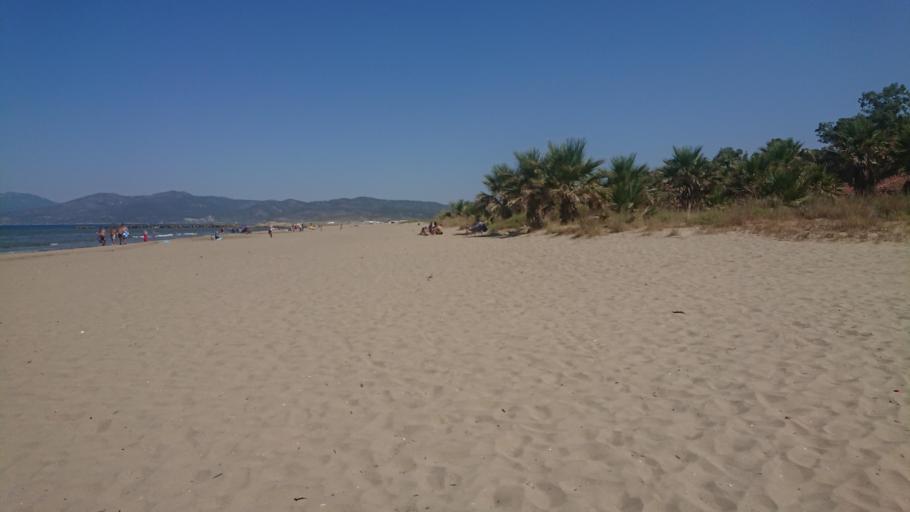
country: TR
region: Aydin
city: Kusadasi
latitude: 37.9384
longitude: 27.2755
